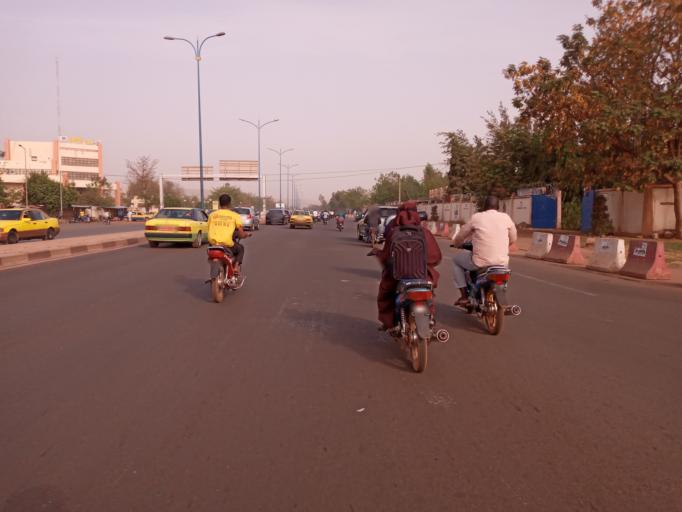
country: ML
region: Bamako
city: Bamako
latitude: 12.6331
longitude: -8.0123
